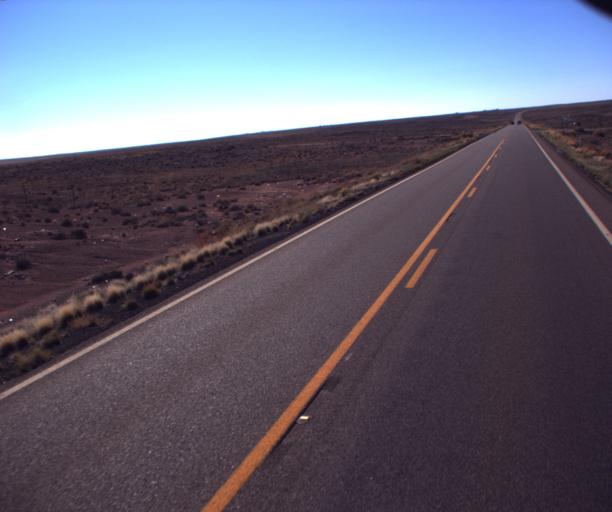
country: US
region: Arizona
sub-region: Navajo County
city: Dilkon
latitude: 35.2511
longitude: -110.4300
